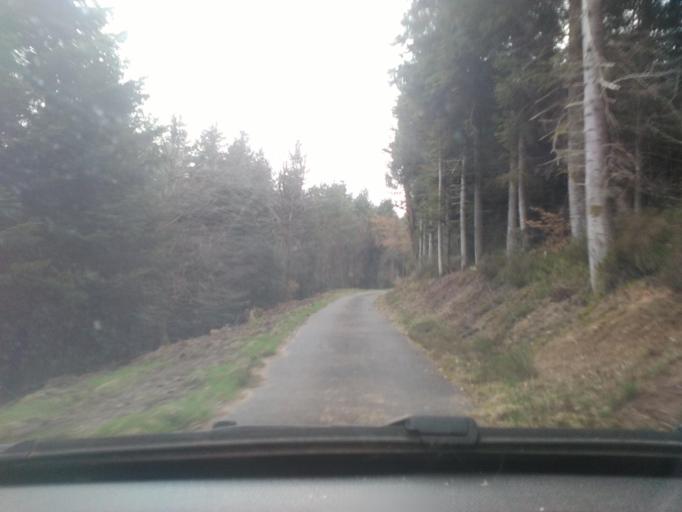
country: FR
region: Lorraine
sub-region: Departement des Vosges
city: Moyenmoutier
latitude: 48.3905
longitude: 6.8938
